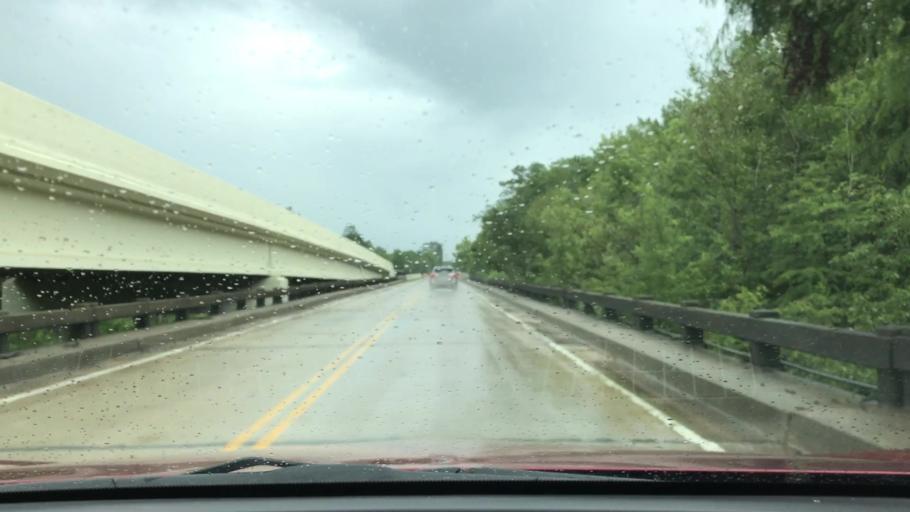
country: US
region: South Carolina
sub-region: Horry County
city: Socastee
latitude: 33.6682
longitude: -79.1434
